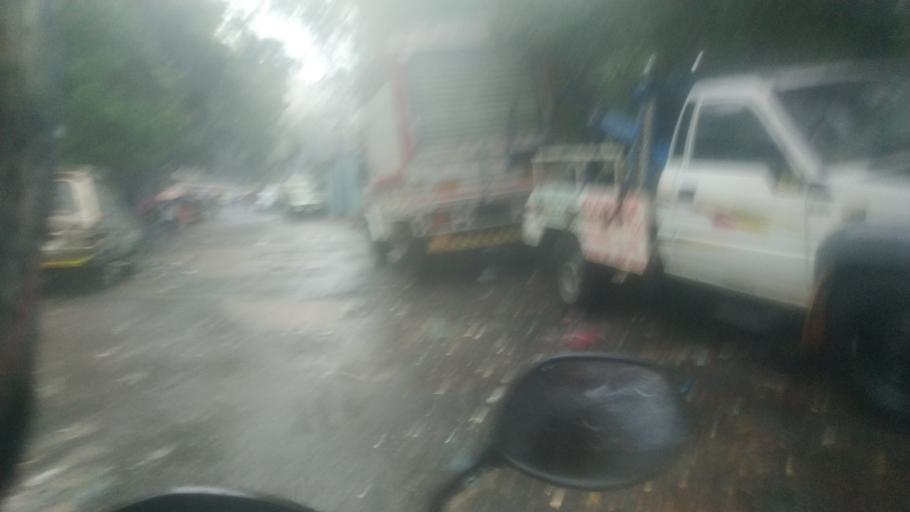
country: IN
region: Maharashtra
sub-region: Mumbai Suburban
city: Mumbai
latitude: 19.1109
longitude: 72.8378
